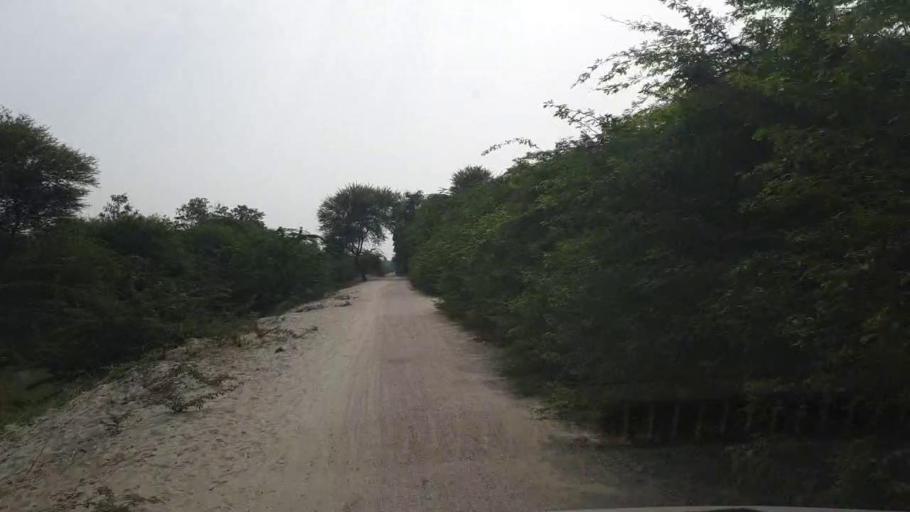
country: PK
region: Sindh
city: Matli
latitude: 25.0041
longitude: 68.7012
